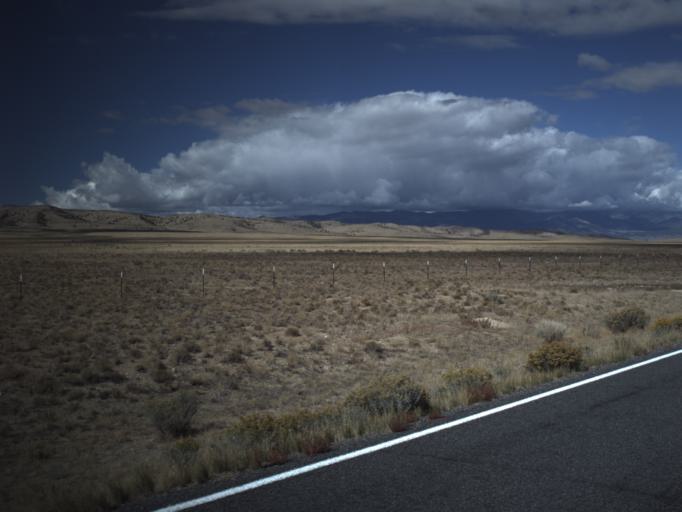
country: US
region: Utah
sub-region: Beaver County
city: Milford
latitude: 38.6748
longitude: -113.8878
